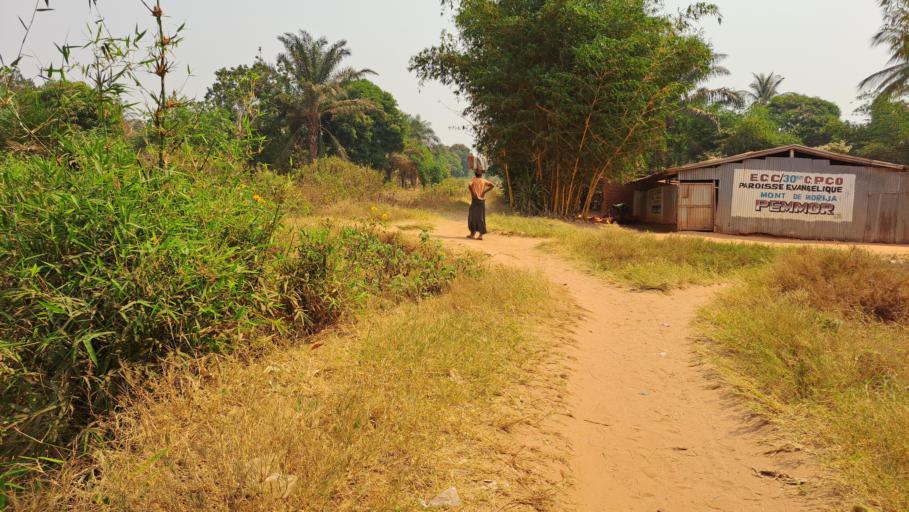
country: CD
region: Kasai-Oriental
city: Mbuji-Mayi
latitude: -6.0987
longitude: 23.5651
